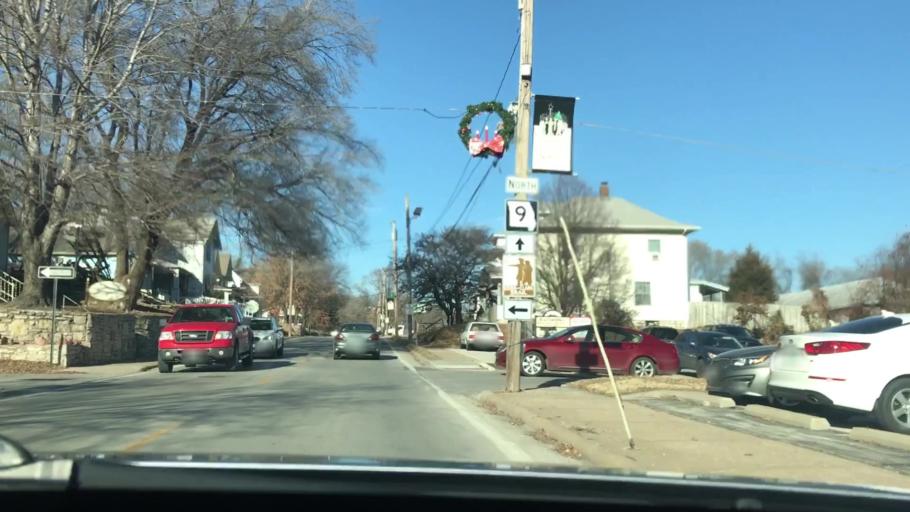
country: US
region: Missouri
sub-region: Platte County
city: Parkville
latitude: 39.1896
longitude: -94.6829
